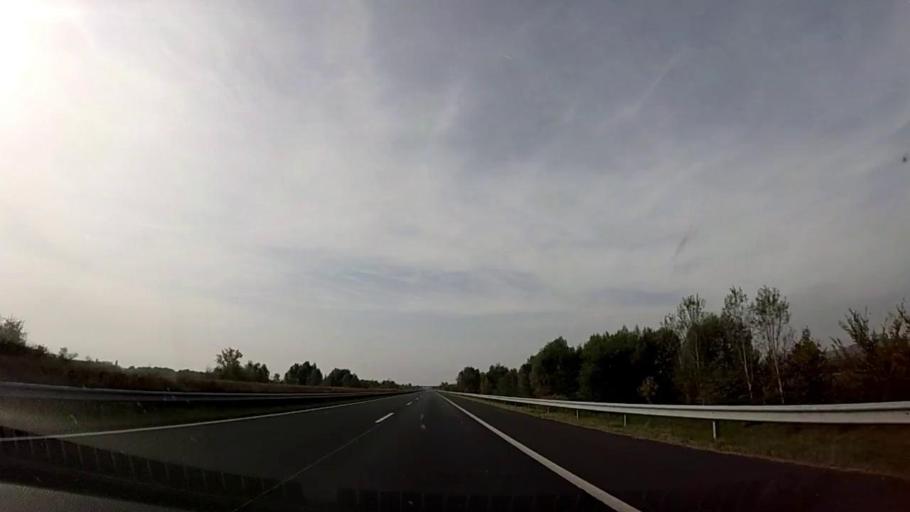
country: HU
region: Somogy
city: Fonyod
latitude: 46.7387
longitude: 17.6035
